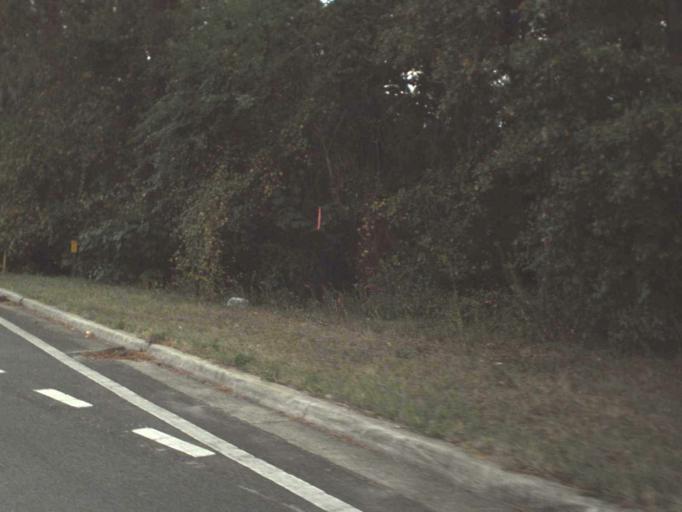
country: US
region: Florida
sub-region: Leon County
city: Tallahassee
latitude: 30.5136
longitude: -84.3448
